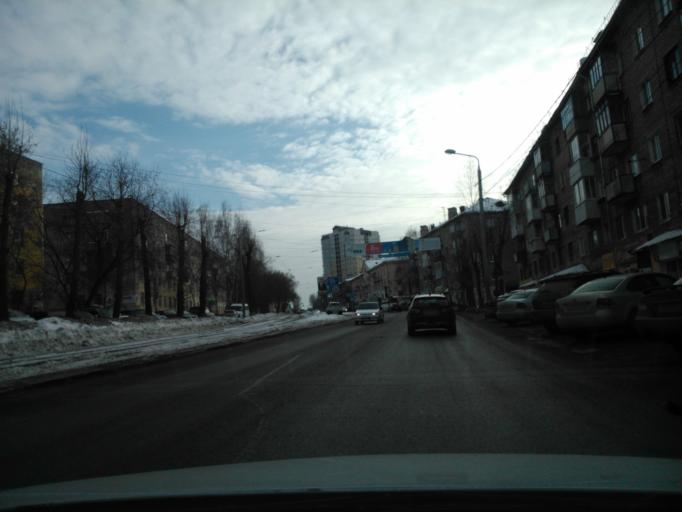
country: RU
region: Perm
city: Perm
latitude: 58.0022
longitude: 56.2386
